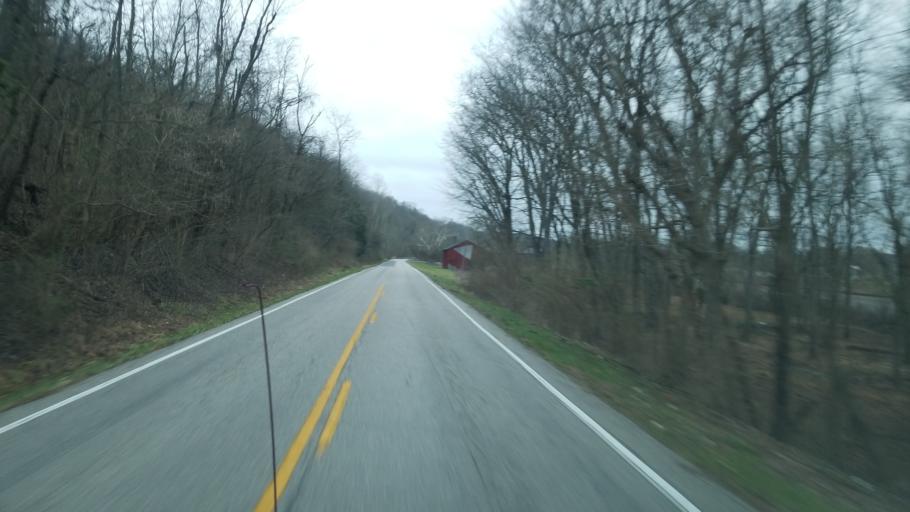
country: US
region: Kentucky
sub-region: Bracken County
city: Augusta
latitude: 38.7675
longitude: -84.0885
